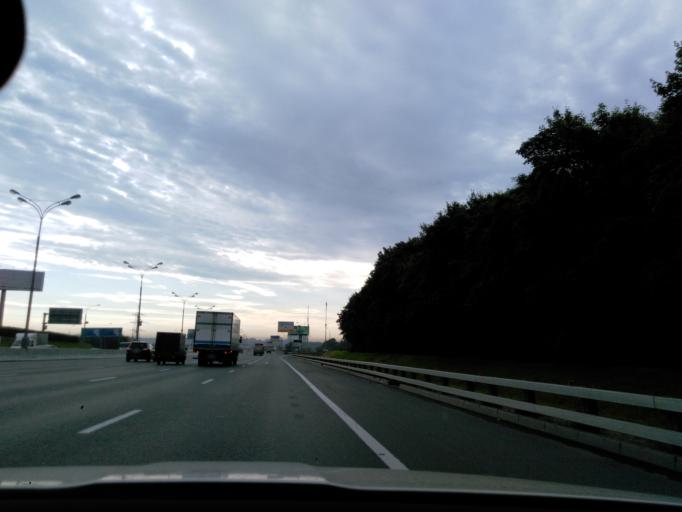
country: RU
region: Moscow
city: Vatutino
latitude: 55.8953
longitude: 37.6658
